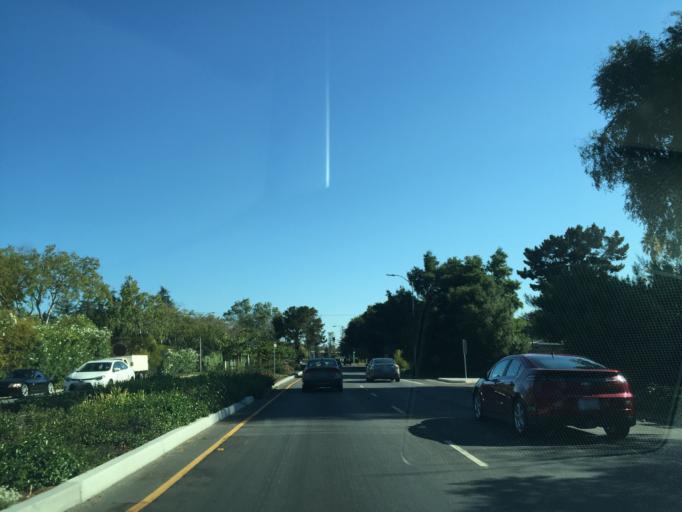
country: US
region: California
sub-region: Santa Clara County
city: Palo Alto
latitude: 37.4437
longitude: -122.1250
